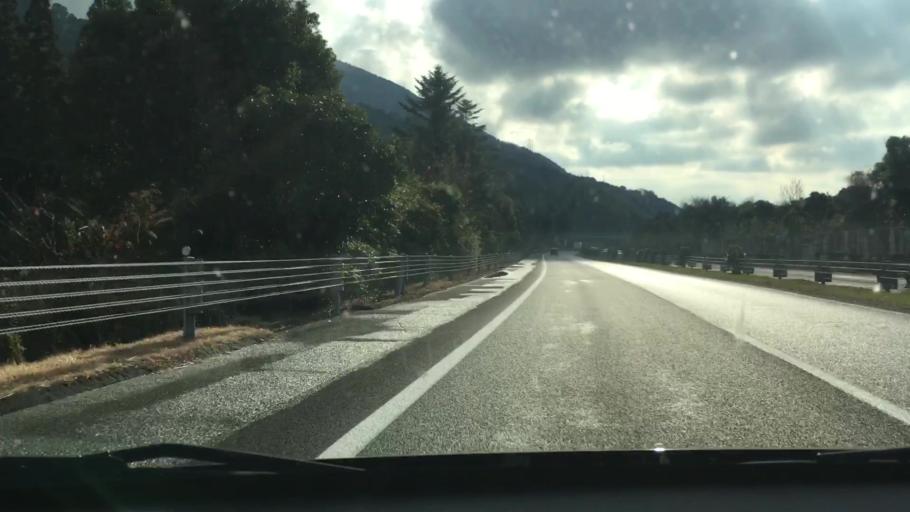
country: JP
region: Kumamoto
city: Yatsushiro
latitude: 32.5360
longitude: 130.6727
